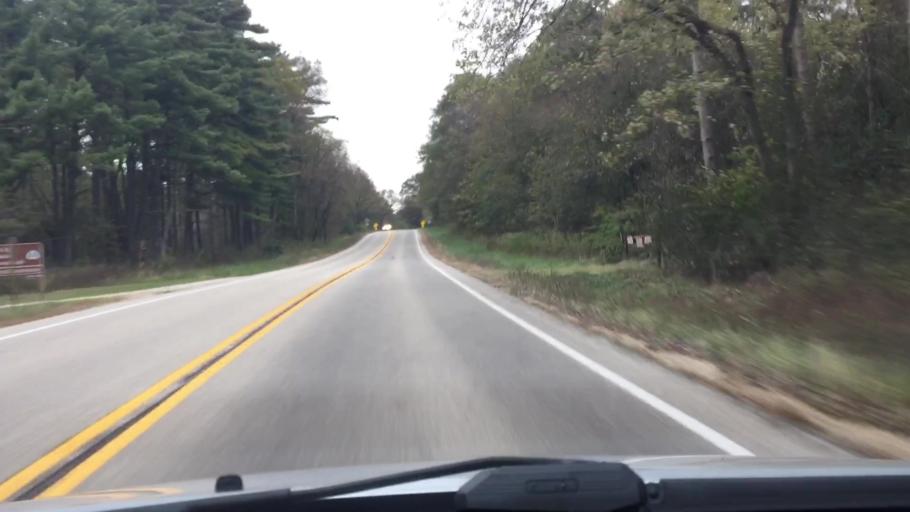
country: US
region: Wisconsin
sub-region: Waukesha County
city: Eagle
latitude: 42.9187
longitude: -88.4730
